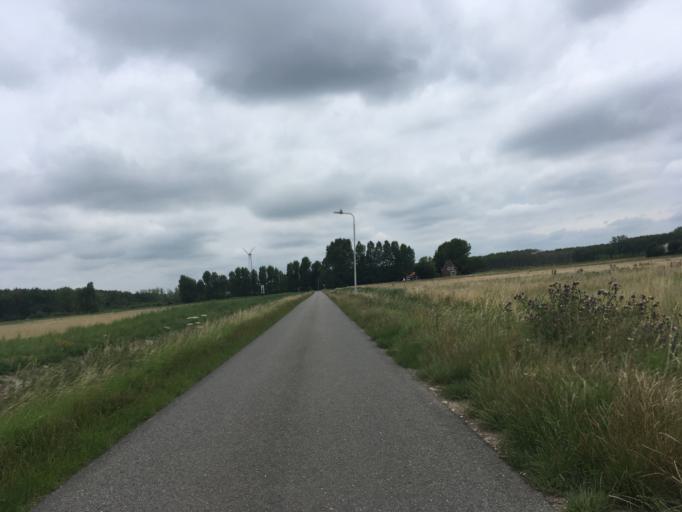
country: NL
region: North Holland
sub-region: Gemeente Velsen
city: Velsen-Zuid
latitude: 52.4214
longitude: 4.7247
